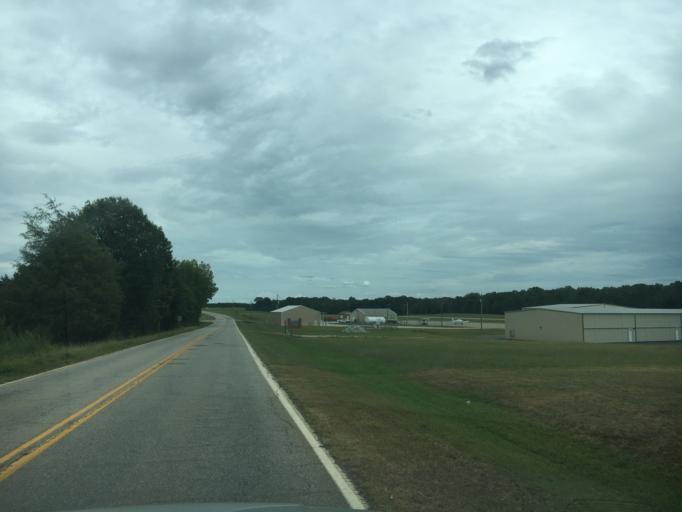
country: US
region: South Carolina
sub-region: Laurens County
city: Watts Mills
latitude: 34.5085
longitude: -81.9511
